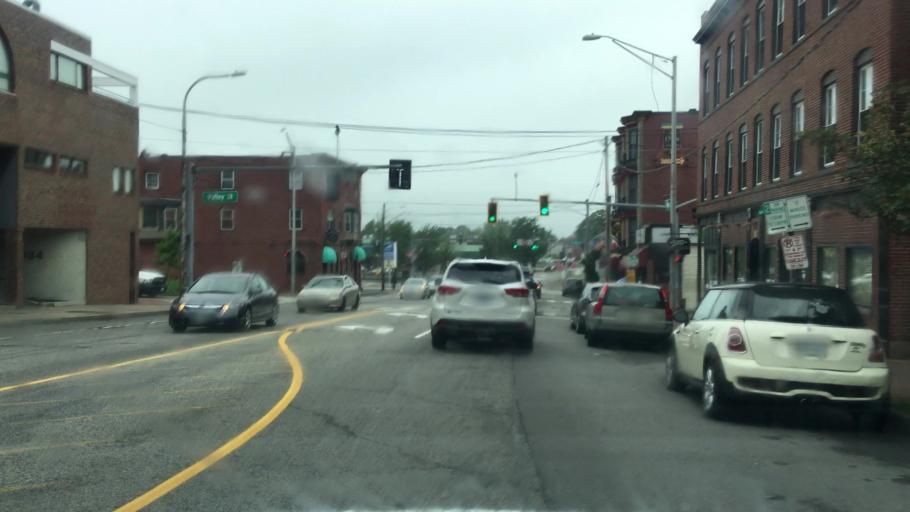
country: US
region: Maine
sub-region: Cumberland County
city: Portland
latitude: 43.6539
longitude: -70.2781
